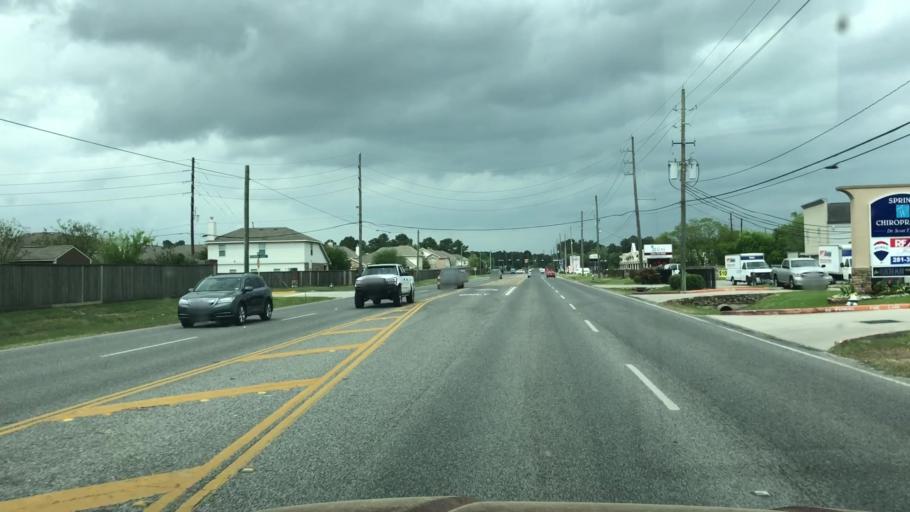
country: US
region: Texas
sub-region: Harris County
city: Spring
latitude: 30.0543
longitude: -95.4943
